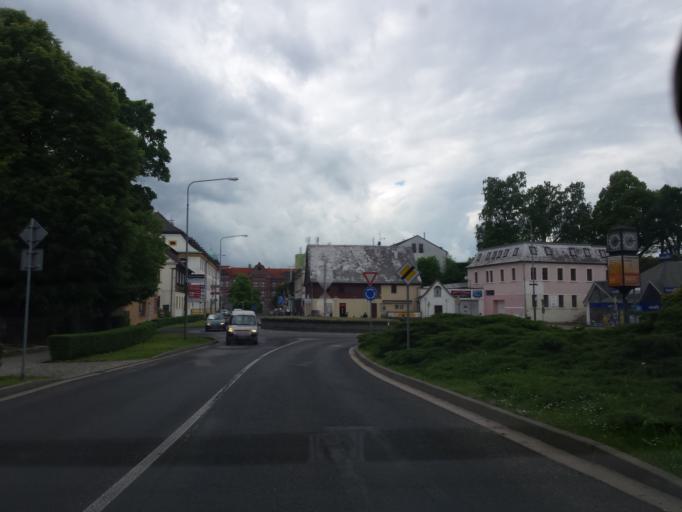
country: CZ
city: Novy Bor
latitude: 50.7612
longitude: 14.5572
